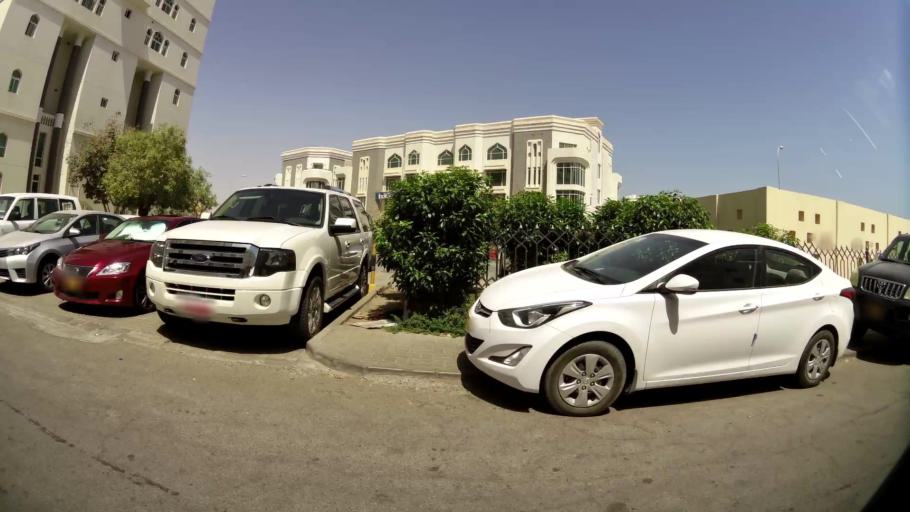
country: OM
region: Muhafazat Masqat
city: Bawshar
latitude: 23.5939
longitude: 58.4492
